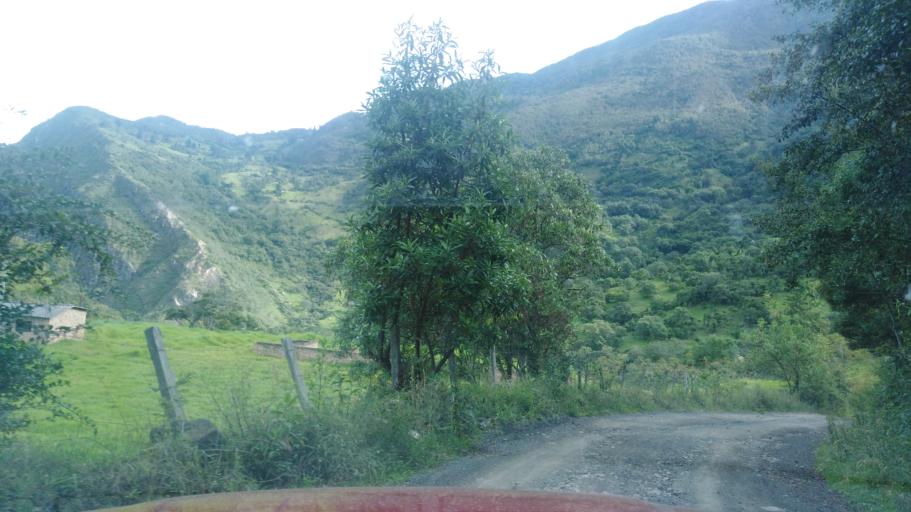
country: CO
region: Boyaca
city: San Mateo
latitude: 6.4206
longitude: -72.5629
